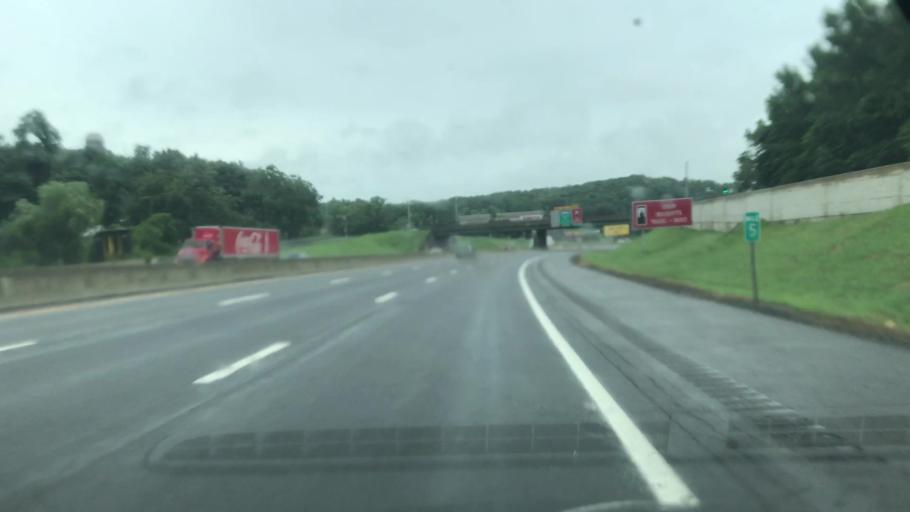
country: US
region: New York
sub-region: Westchester County
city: Hastings-on-Hudson
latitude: 40.9695
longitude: -73.8614
